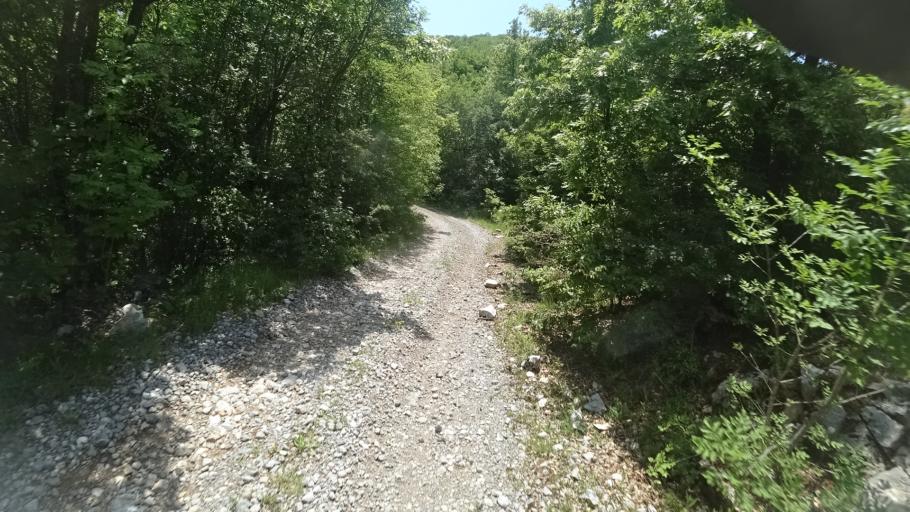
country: HR
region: Zadarska
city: Gracac
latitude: 44.4453
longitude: 15.9126
